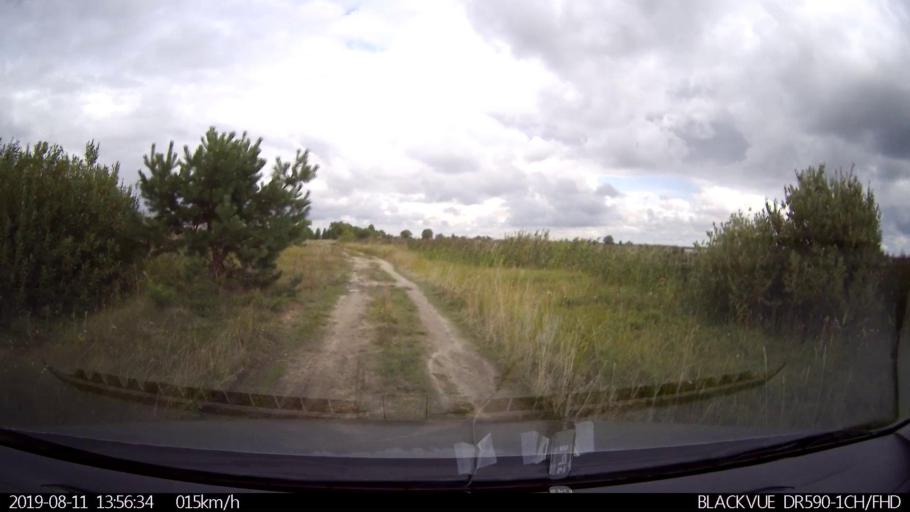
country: RU
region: Ulyanovsk
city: Ignatovka
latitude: 53.8480
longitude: 47.5889
